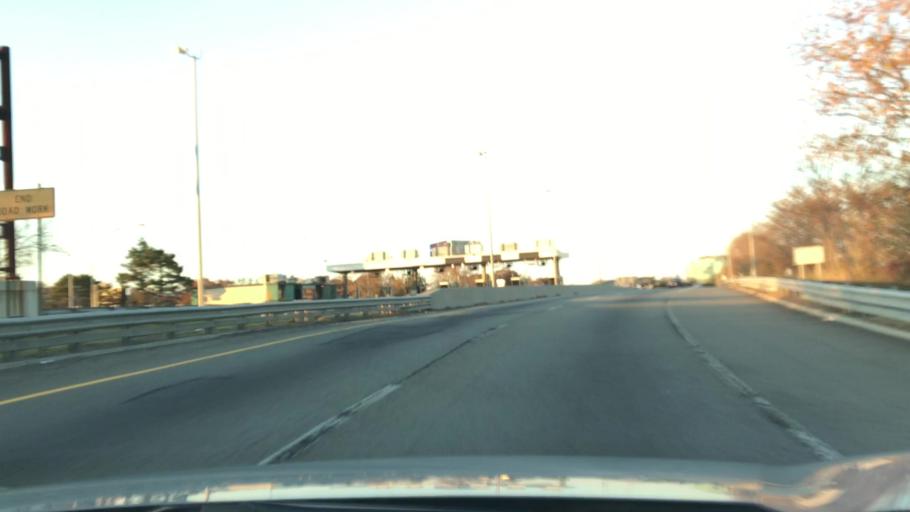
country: US
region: New Jersey
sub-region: Hudson County
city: Secaucus
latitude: 40.7813
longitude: -74.0522
